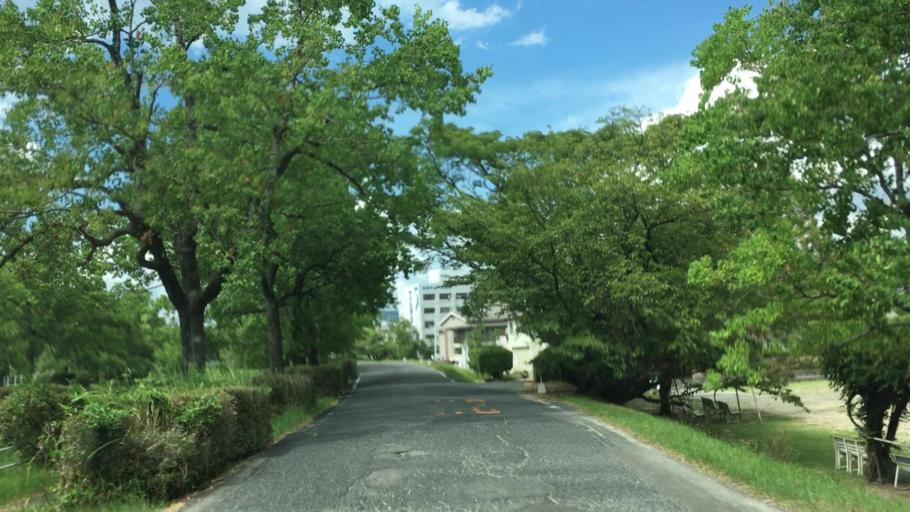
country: JP
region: Saga Prefecture
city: Saga-shi
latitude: 33.2712
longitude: 130.2825
